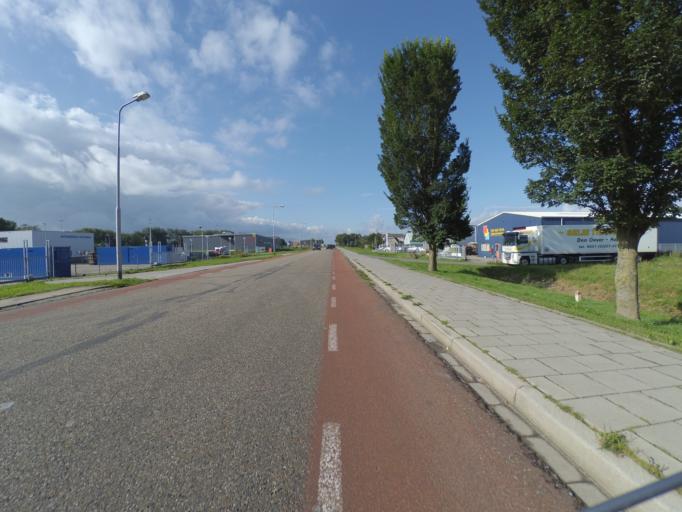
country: NL
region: North Holland
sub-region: Gemeente Hollands Kroon
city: Den Oever
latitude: 52.9313
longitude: 5.0338
